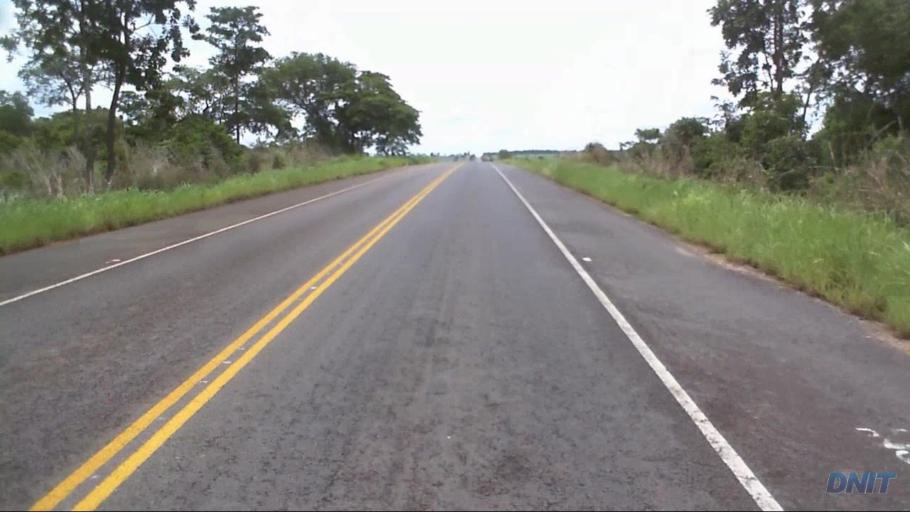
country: BR
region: Goias
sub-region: Sao Miguel Do Araguaia
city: Sao Miguel do Araguaia
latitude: -13.3020
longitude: -50.2800
